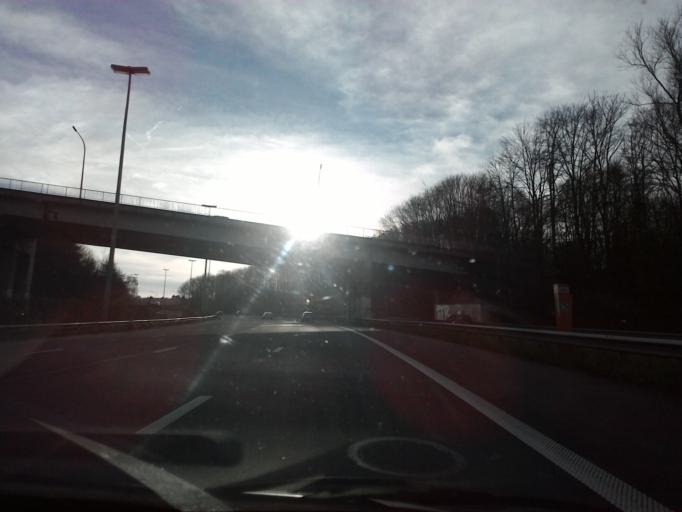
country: BE
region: Wallonia
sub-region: Province de Liege
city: Chaudfontaine
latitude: 50.5632
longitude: 5.5986
